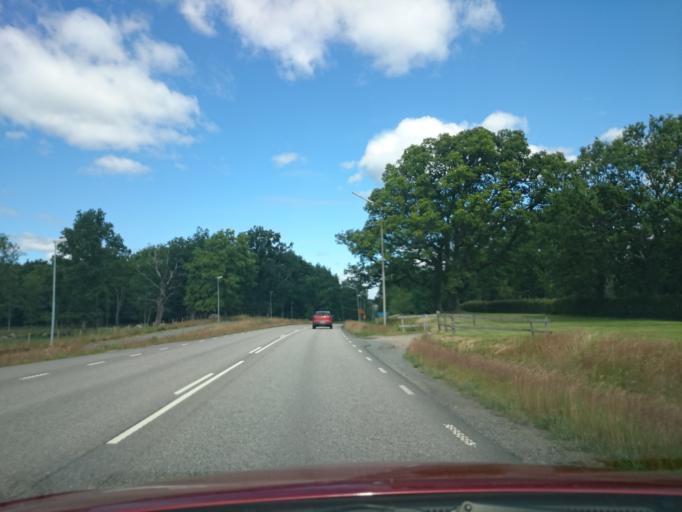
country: SE
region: Vaestra Goetaland
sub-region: Lerums Kommun
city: Grabo
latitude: 57.8279
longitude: 12.2911
